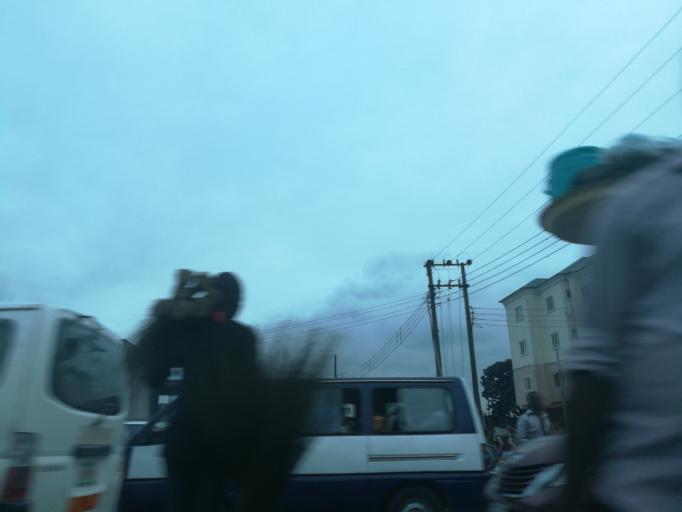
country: NG
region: Rivers
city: Port Harcourt
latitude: 4.8018
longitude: 6.9904
